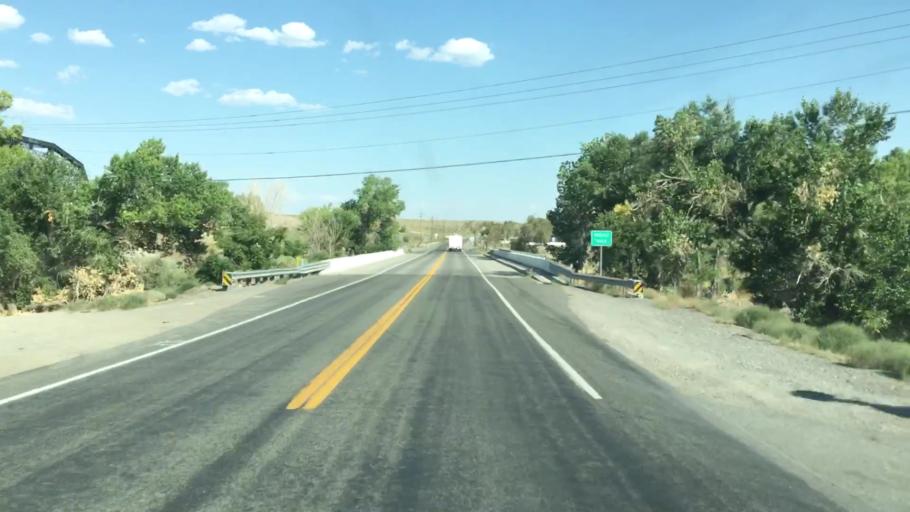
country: US
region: Nevada
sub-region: Lyon County
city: Fernley
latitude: 39.6323
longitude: -119.2841
